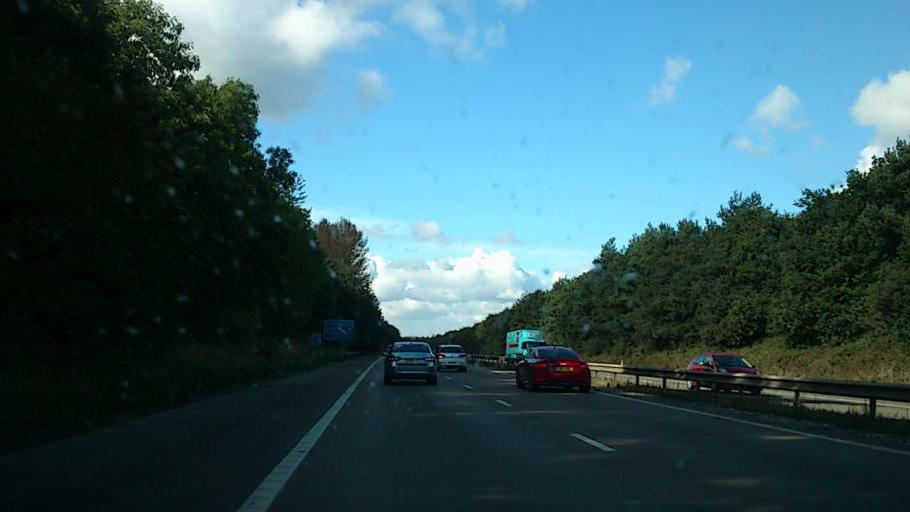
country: GB
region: England
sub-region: Shropshire
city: Albrighton
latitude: 52.6542
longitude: -2.2778
